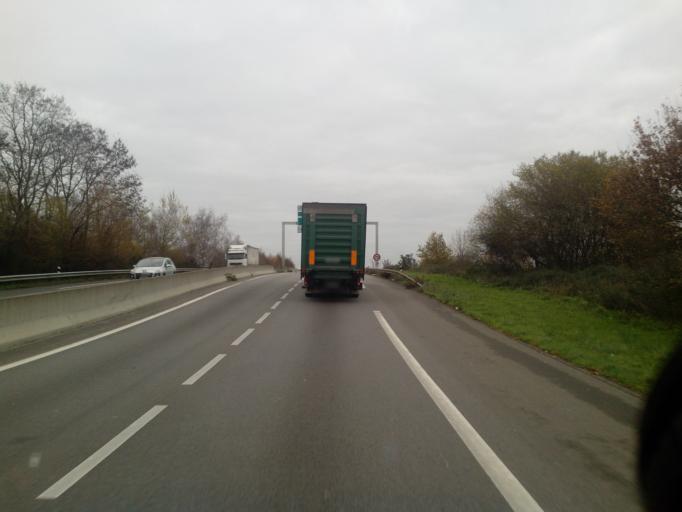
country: FR
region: Pays de la Loire
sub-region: Departement de la Loire-Atlantique
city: Sainte-Luce-sur-Loire
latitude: 47.2396
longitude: -1.4862
